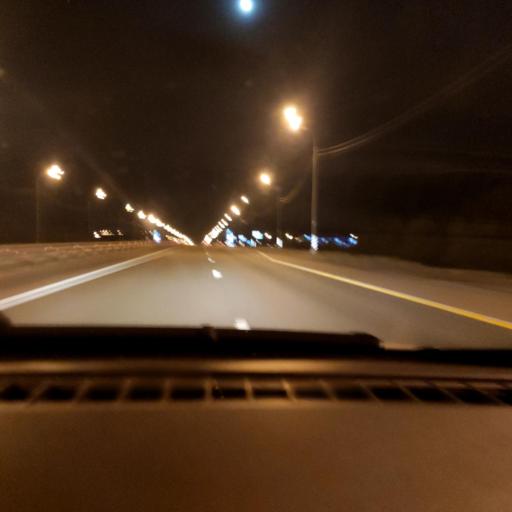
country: RU
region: Lipetsk
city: Khlevnoye
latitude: 52.2323
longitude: 39.0872
